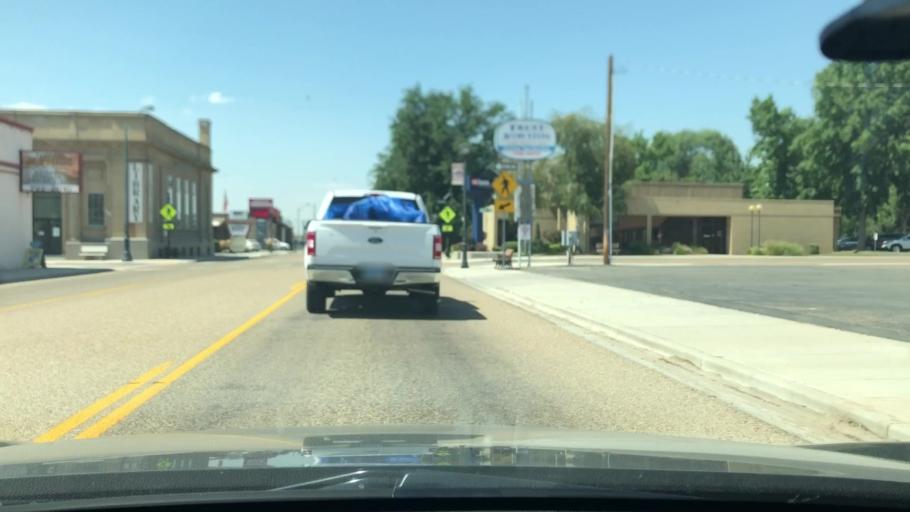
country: US
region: Idaho
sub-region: Canyon County
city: Parma
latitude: 43.7854
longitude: -116.9436
